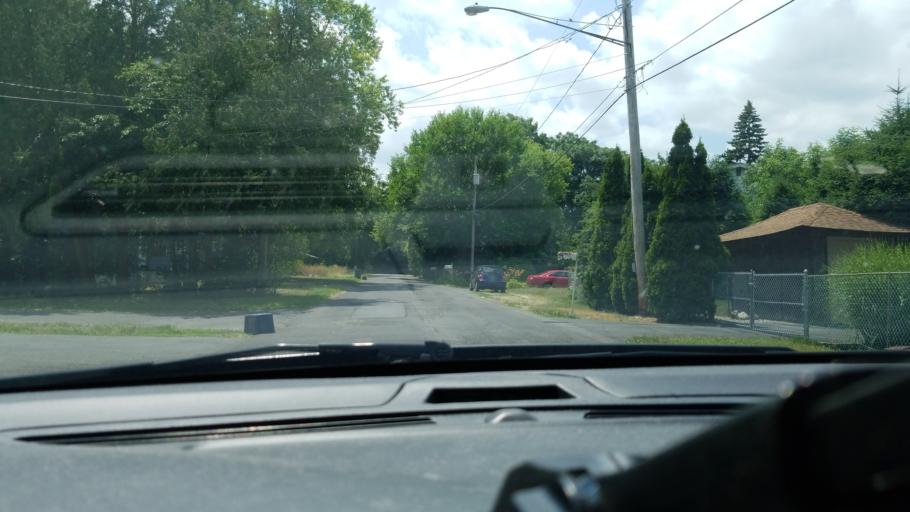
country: US
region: New York
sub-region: Onondaga County
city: Galeville
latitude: 43.0884
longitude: -76.1691
